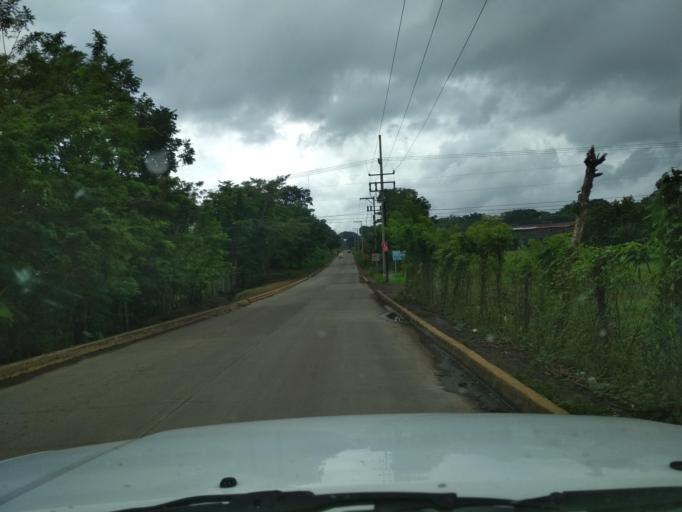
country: MX
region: Veracruz
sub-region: San Andres Tuxtla
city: Matacapan
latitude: 18.4250
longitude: -95.1773
